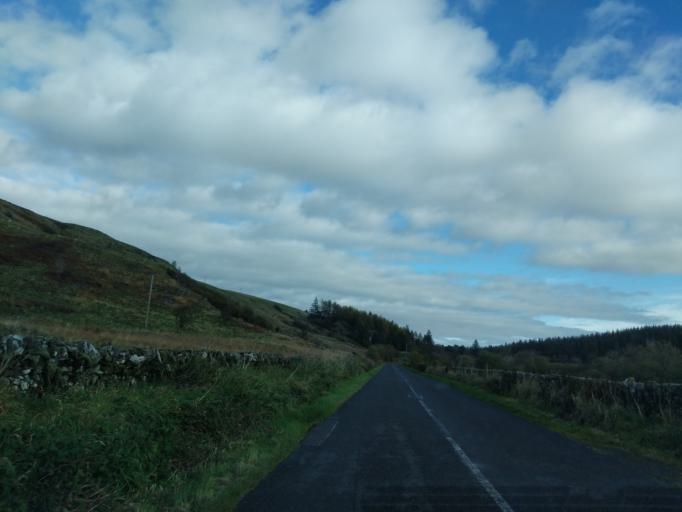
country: GB
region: Scotland
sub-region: Dumfries and Galloway
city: Sanquhar
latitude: 55.1711
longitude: -3.9565
